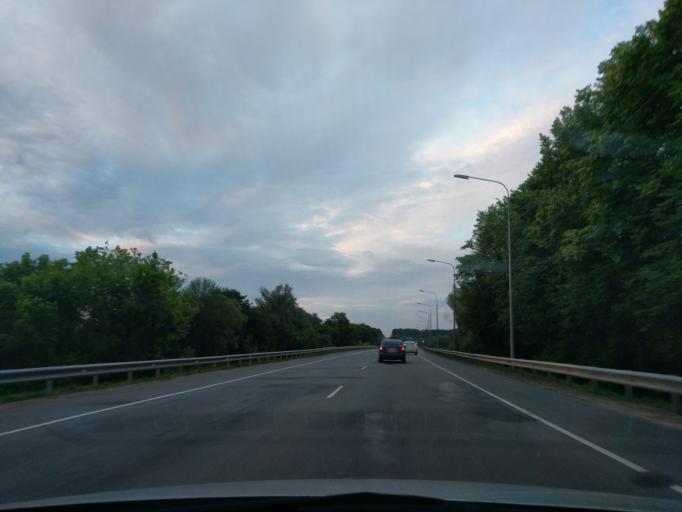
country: RU
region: Kaluga
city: Obninsk
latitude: 55.0564
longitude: 36.5768
